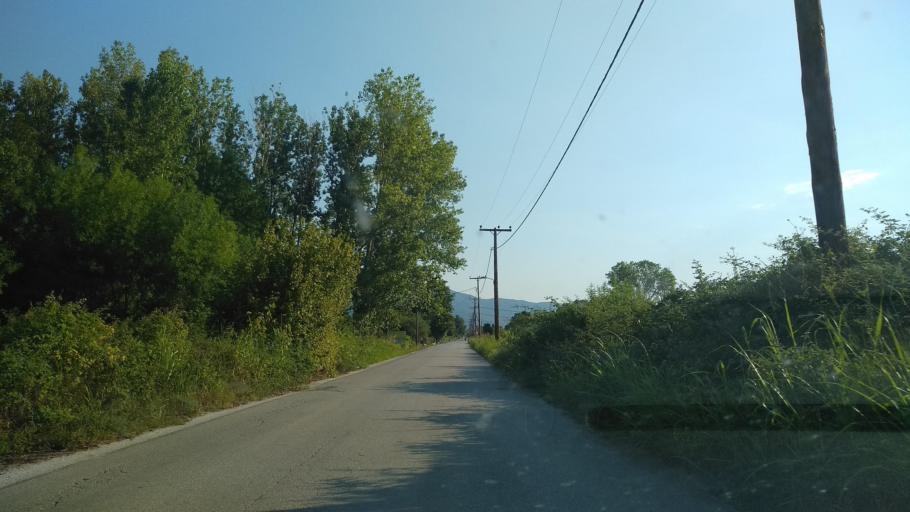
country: GR
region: Central Macedonia
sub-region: Nomos Thessalonikis
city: Stavros
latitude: 40.6806
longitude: 23.6870
